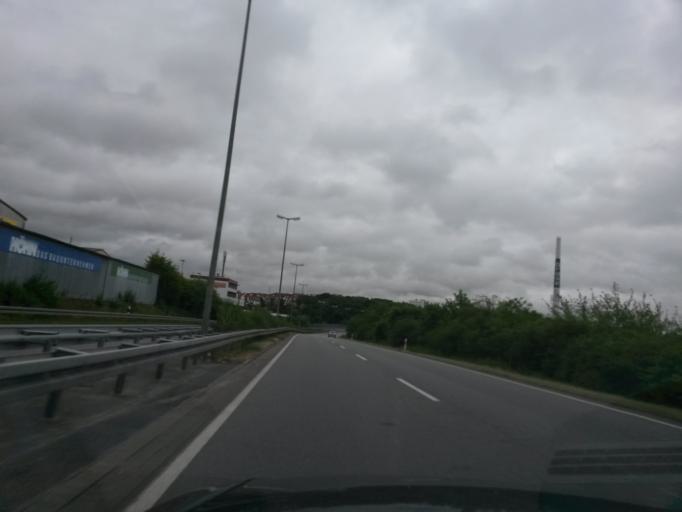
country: DE
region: Bavaria
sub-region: Regierungsbezirk Unterfranken
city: Wuerzburg
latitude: 49.7990
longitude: 9.9721
